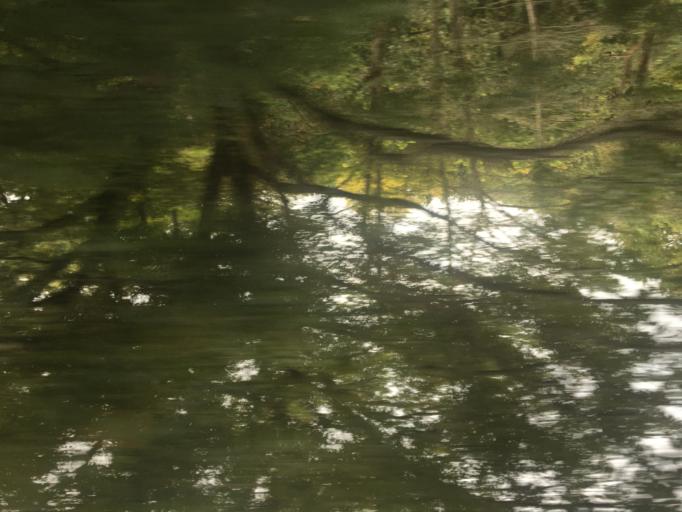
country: JP
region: Tokyo
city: Fussa
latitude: 35.7940
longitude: 139.3371
